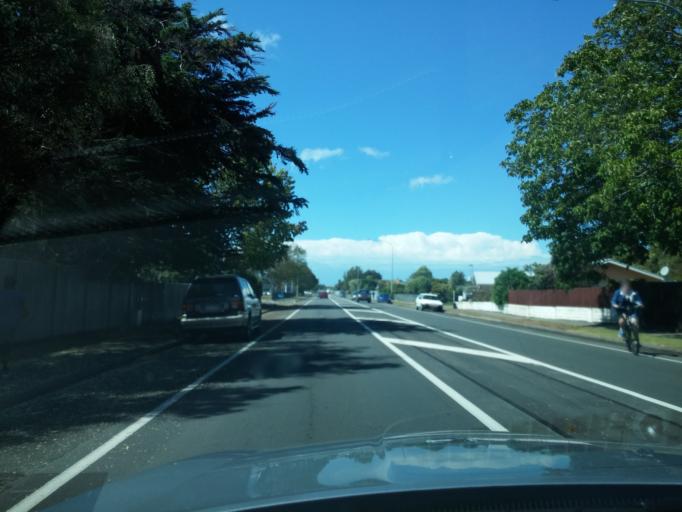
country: NZ
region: Marlborough
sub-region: Marlborough District
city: Blenheim
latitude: -41.5088
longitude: 173.9420
